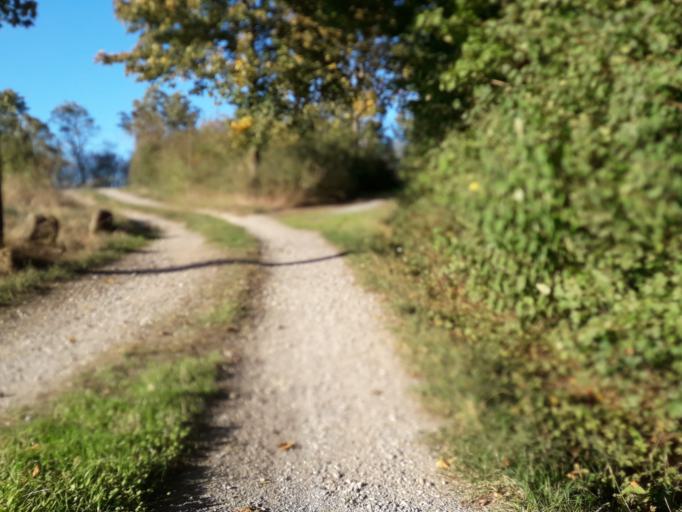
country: DE
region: North Rhine-Westphalia
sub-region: Regierungsbezirk Detmold
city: Schlangen
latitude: 51.7822
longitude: 8.8506
